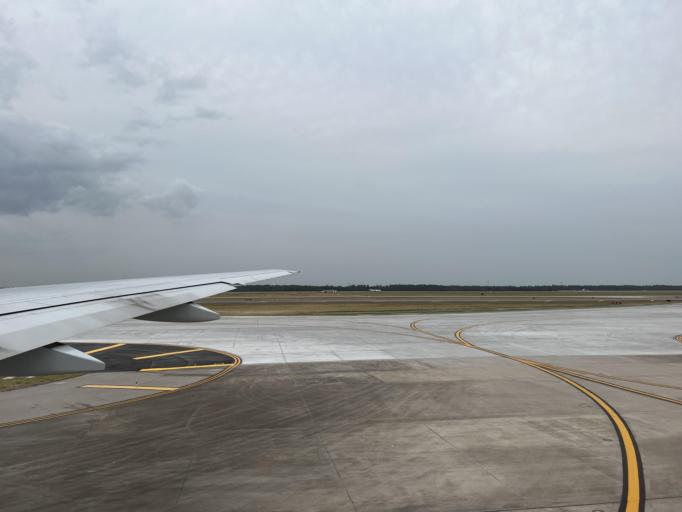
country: US
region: Texas
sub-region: Harris County
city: Aldine
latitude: 29.9908
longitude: -95.3437
